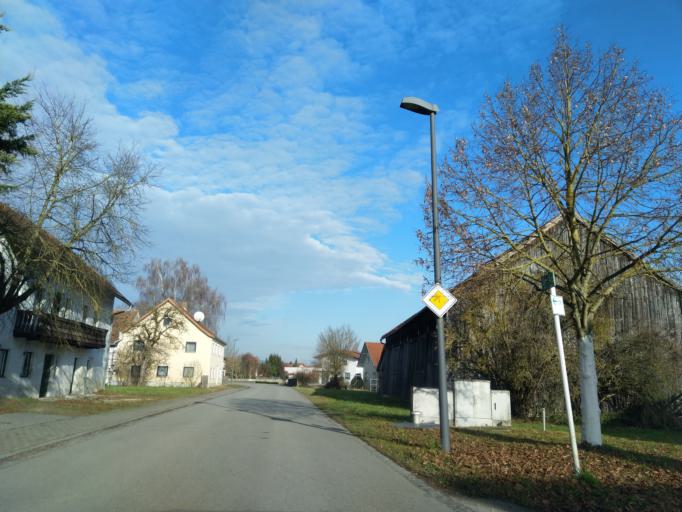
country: DE
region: Bavaria
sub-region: Lower Bavaria
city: Aholming
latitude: 48.7422
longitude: 12.9091
